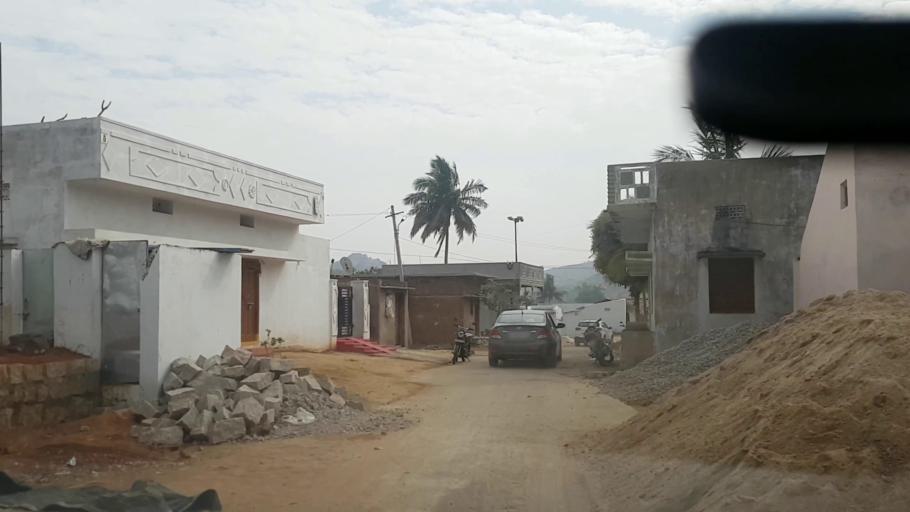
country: IN
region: Telangana
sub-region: Rangareddi
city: Lal Bahadur Nagar
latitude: 17.1709
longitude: 78.7811
